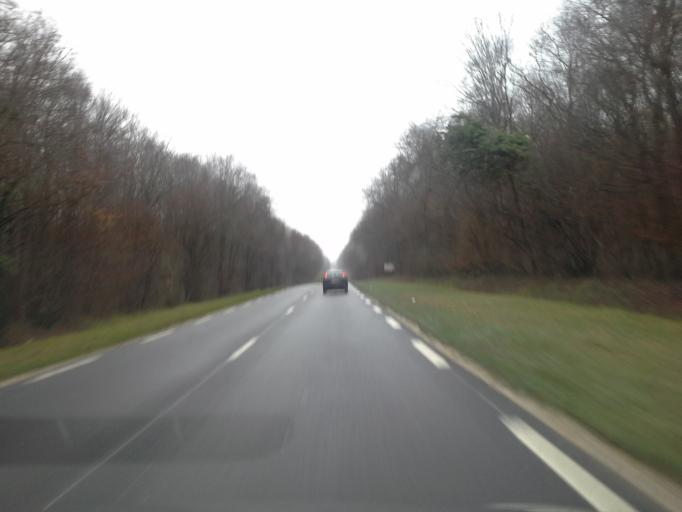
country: FR
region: Centre
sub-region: Departement du Loir-et-Cher
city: Cellettes
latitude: 47.5484
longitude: 1.3743
